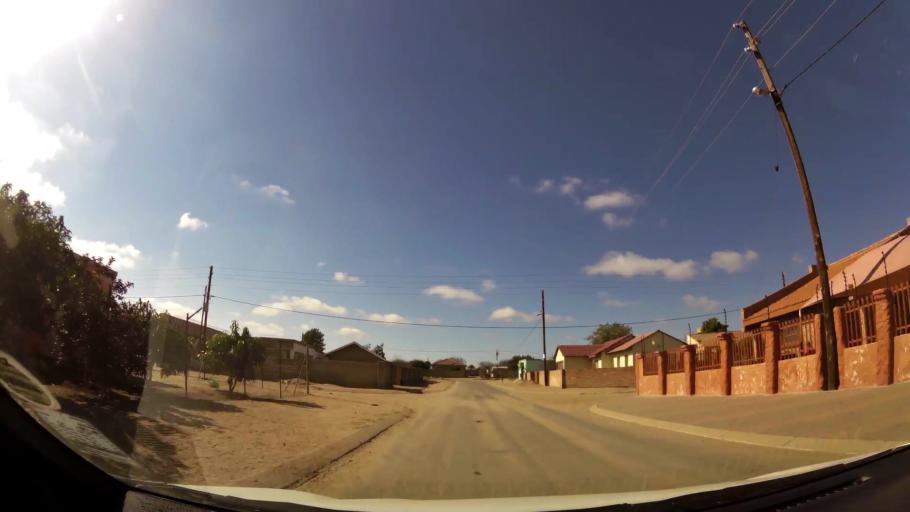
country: ZA
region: Limpopo
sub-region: Capricorn District Municipality
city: Polokwane
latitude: -23.8616
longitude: 29.3701
